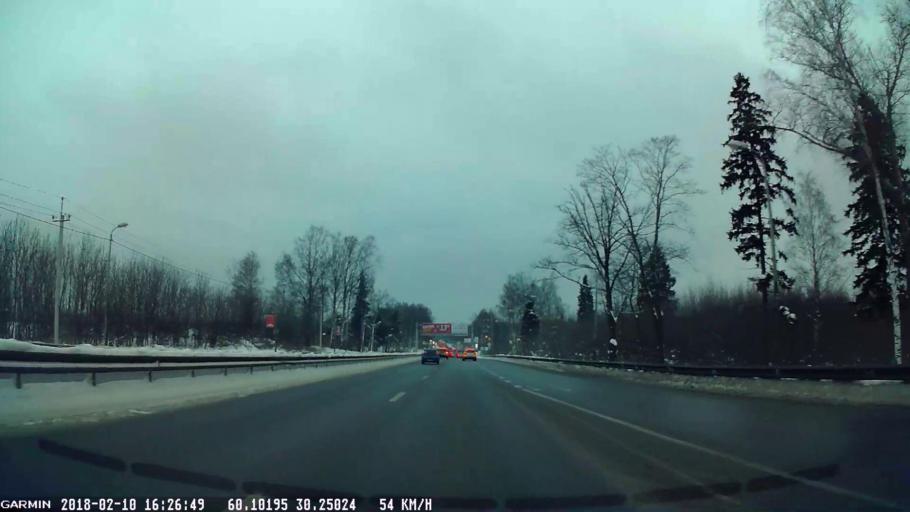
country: RU
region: St.-Petersburg
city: Pargolovo
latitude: 60.1020
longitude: 30.2502
